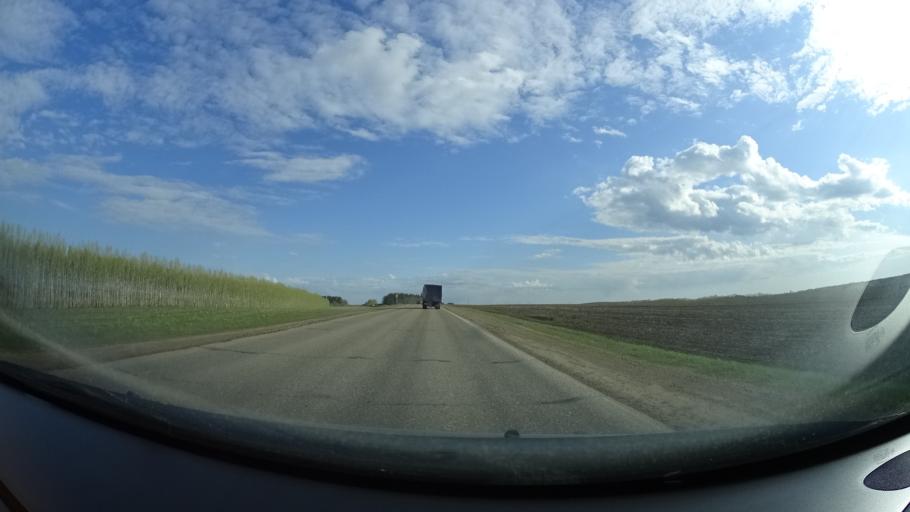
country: RU
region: Bashkortostan
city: Blagoveshchensk
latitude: 55.1481
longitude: 55.8516
